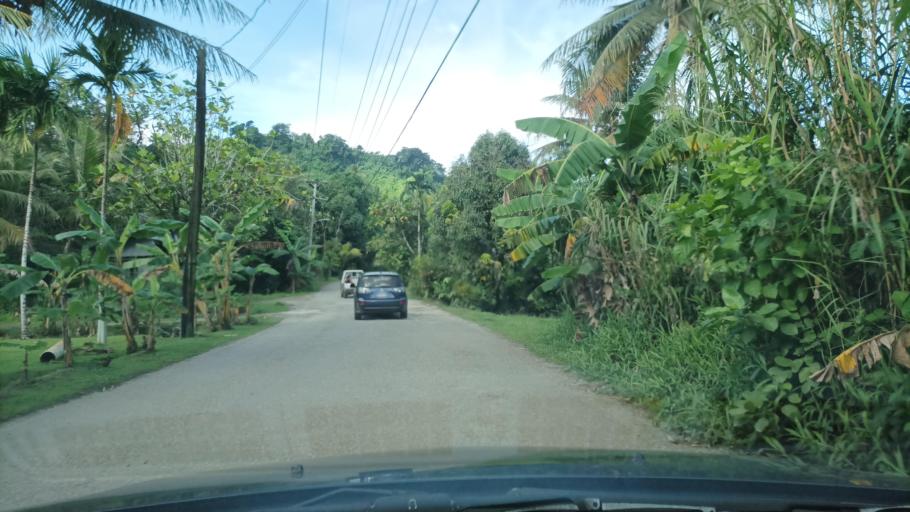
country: FM
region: Kosrae
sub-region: Lelu Municipality
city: Lelu
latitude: 5.3369
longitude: 163.0118
